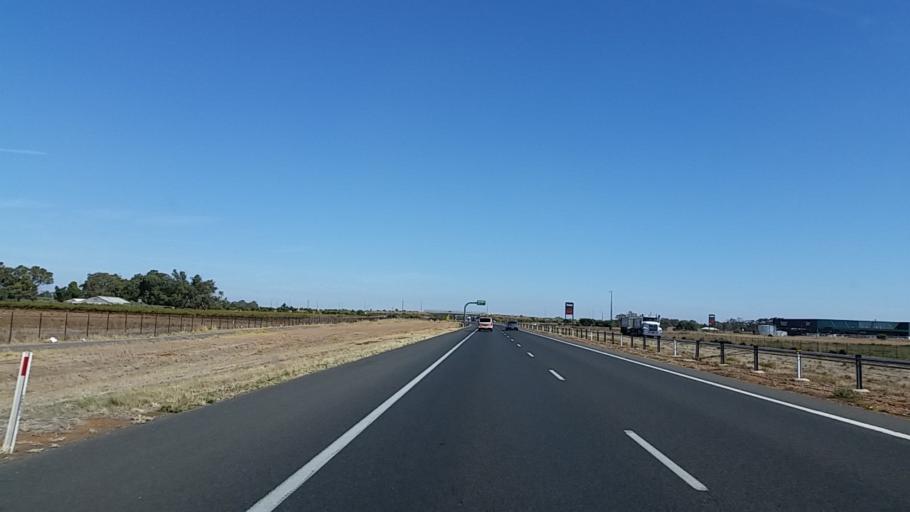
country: AU
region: South Australia
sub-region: Playford
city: Angle Vale
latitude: -34.6566
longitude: 138.6589
